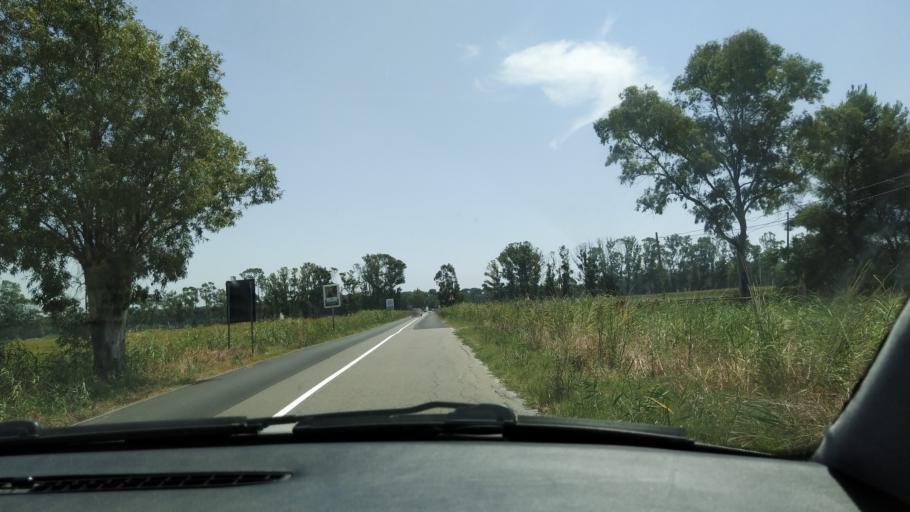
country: IT
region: Basilicate
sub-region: Provincia di Matera
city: Marconia
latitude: 40.3271
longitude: 16.7882
